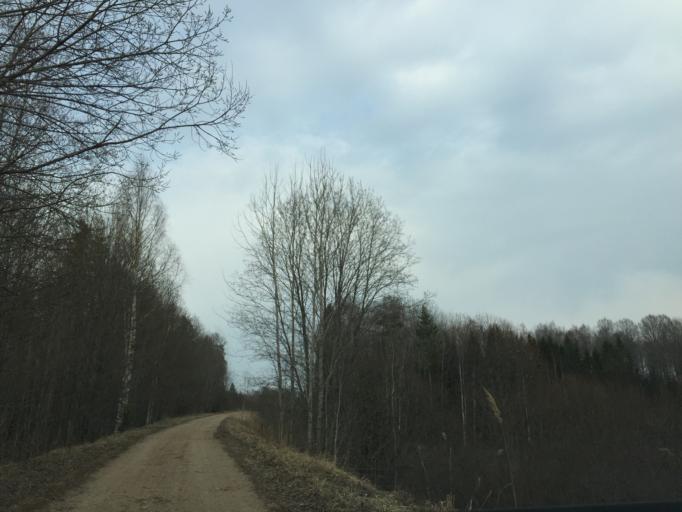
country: LV
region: Priekuli
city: Priekuli
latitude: 57.2054
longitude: 25.3919
